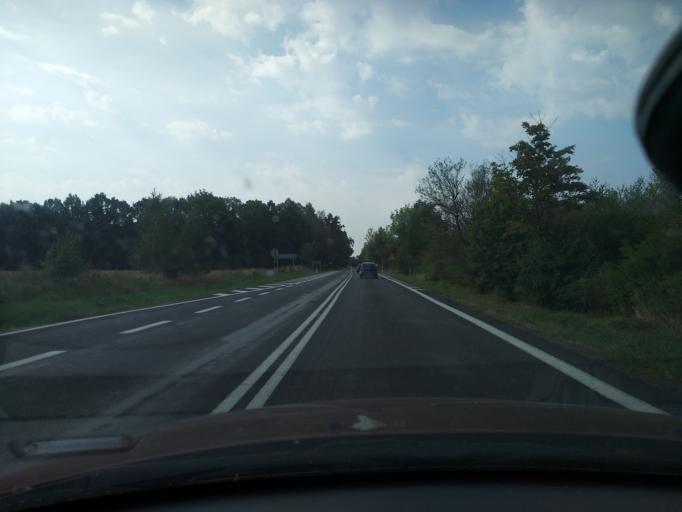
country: PL
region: Lower Silesian Voivodeship
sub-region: Powiat lubanski
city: Olszyna
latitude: 51.0525
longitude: 15.3727
